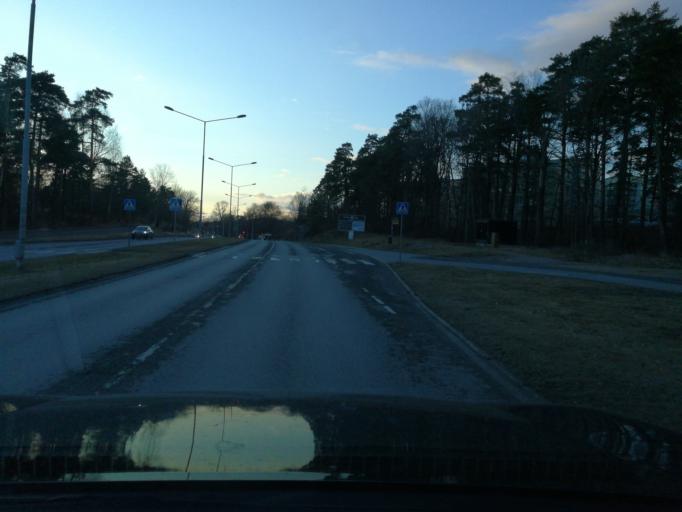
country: FI
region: Varsinais-Suomi
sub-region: Turku
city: Turku
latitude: 60.4333
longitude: 22.2991
